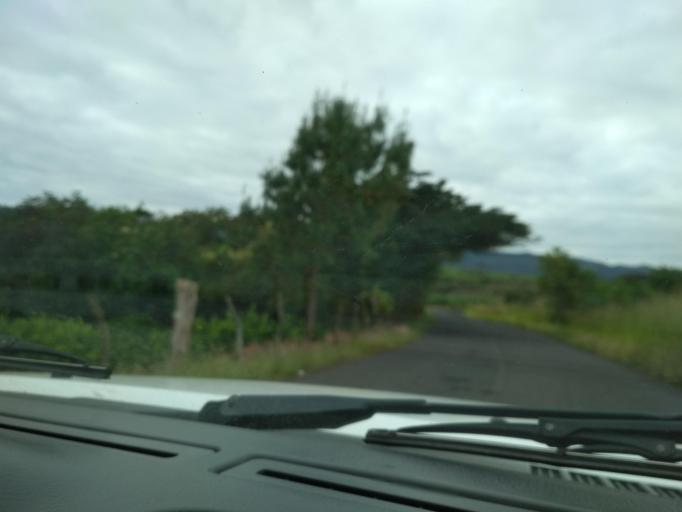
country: MX
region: Veracruz
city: El Castillo
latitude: 19.5849
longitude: -96.8095
